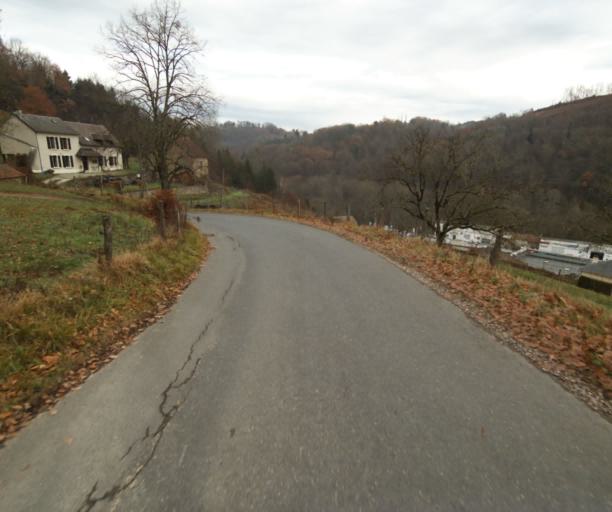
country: FR
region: Limousin
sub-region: Departement de la Correze
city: Tulle
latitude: 45.2432
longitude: 1.7415
